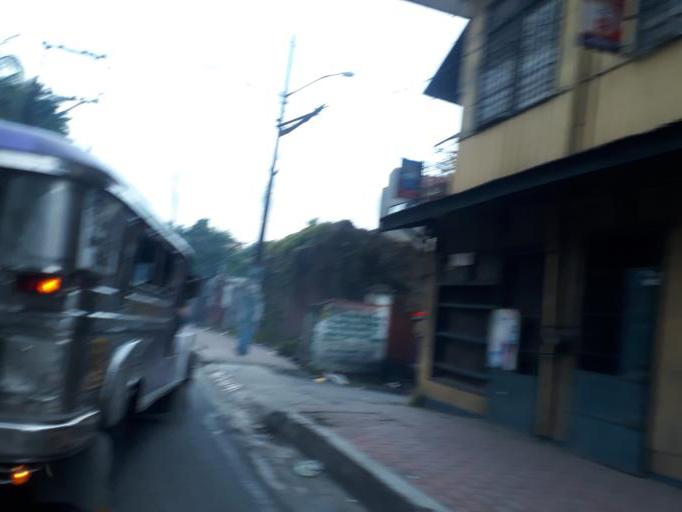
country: PH
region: Calabarzon
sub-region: Province of Rizal
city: Valenzuela
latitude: 14.6901
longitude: 120.9625
